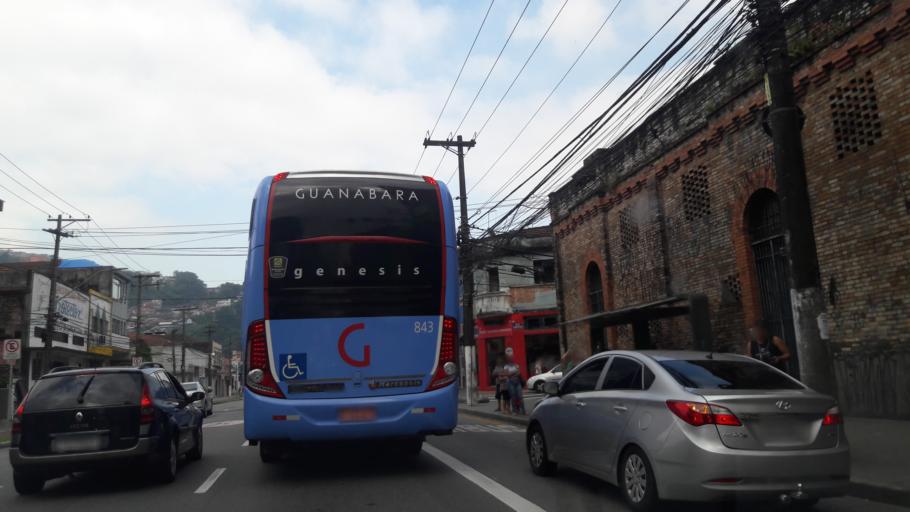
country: BR
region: Sao Paulo
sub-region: Santos
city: Santos
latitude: -23.9336
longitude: -46.3322
